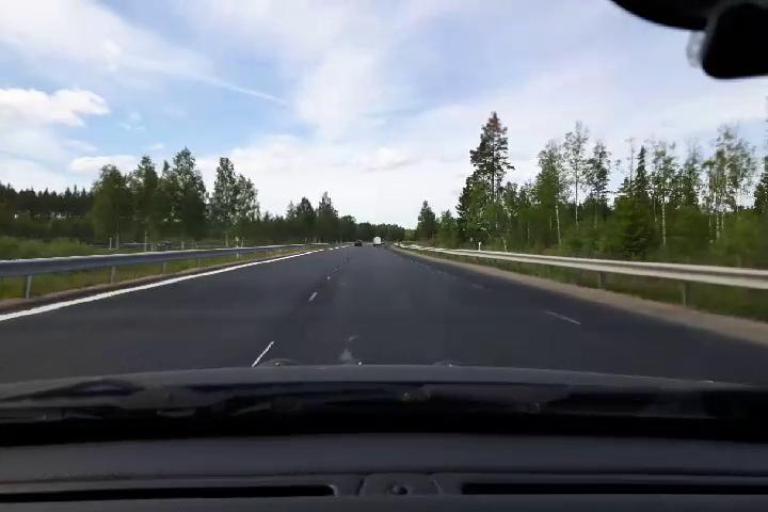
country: SE
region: Gaevleborg
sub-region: Gavle Kommun
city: Gavle
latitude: 60.5838
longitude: 17.2064
